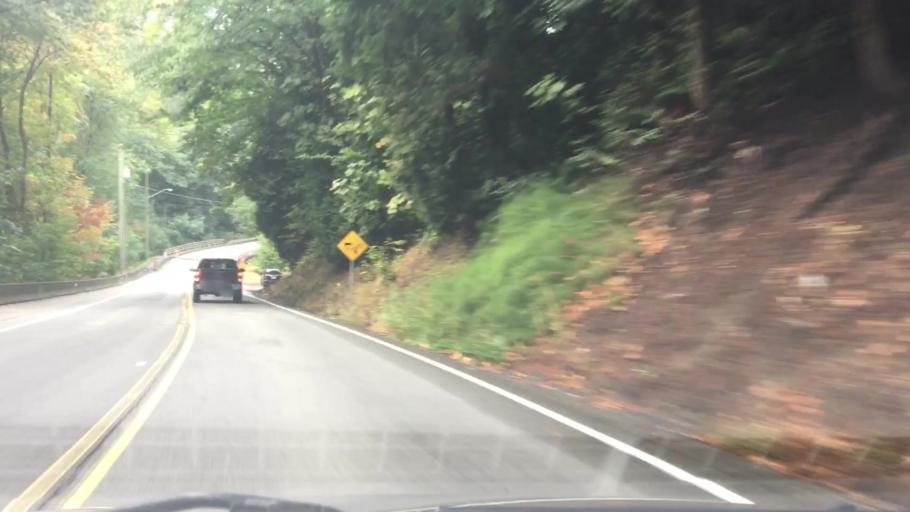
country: CA
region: British Columbia
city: Langley
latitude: 49.1029
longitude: -122.5466
